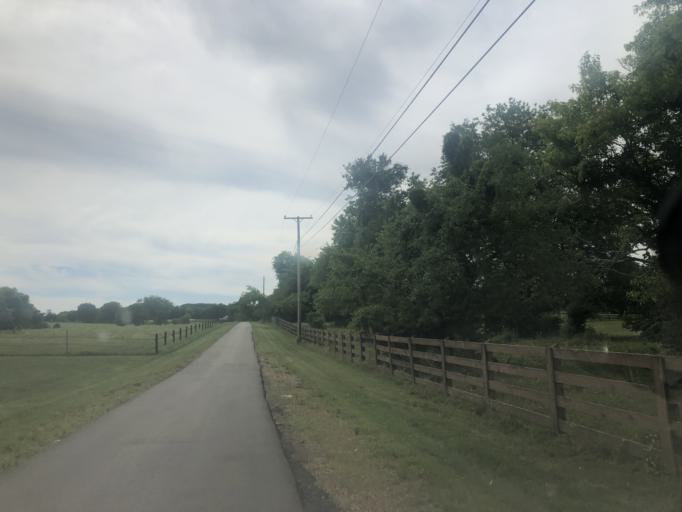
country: US
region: Tennessee
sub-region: Davidson County
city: Lakewood
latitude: 36.2250
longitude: -86.6502
